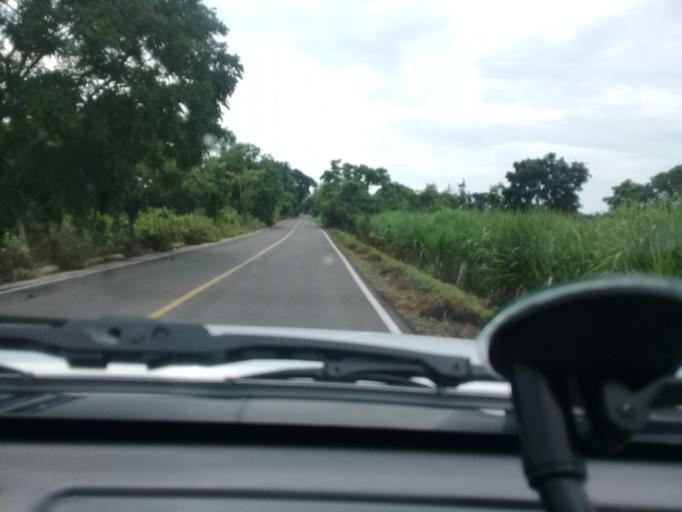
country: MX
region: Veracruz
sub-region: Paso de Ovejas
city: El Hatito
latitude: 19.3086
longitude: -96.4109
